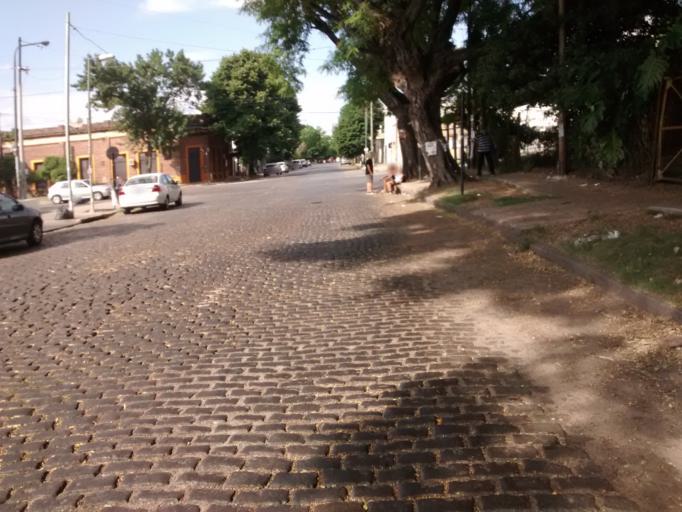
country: AR
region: Buenos Aires
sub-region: Partido de La Plata
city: La Plata
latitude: -34.9362
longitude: -57.9356
